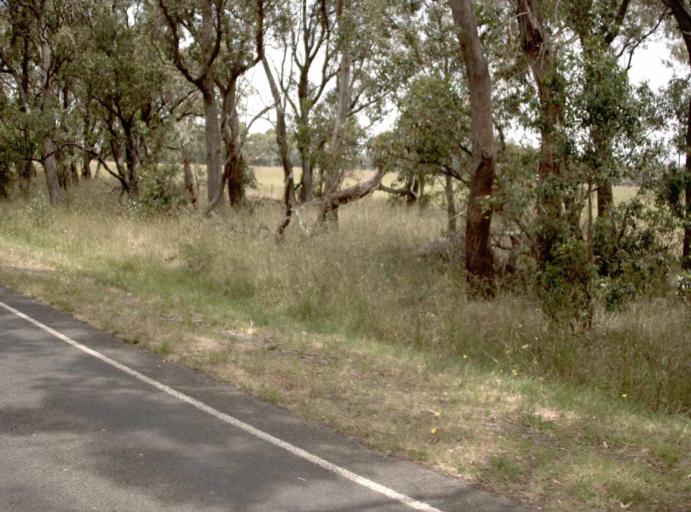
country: AU
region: Victoria
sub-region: Latrobe
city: Traralgon
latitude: -38.4898
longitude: 146.7135
